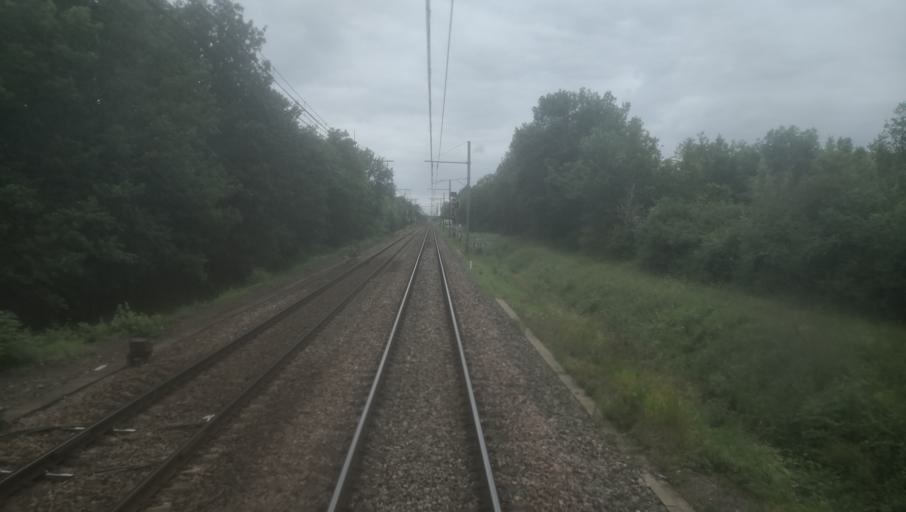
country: FR
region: Midi-Pyrenees
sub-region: Departement du Tarn-et-Garonne
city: Finhan
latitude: 43.8985
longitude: 1.2677
